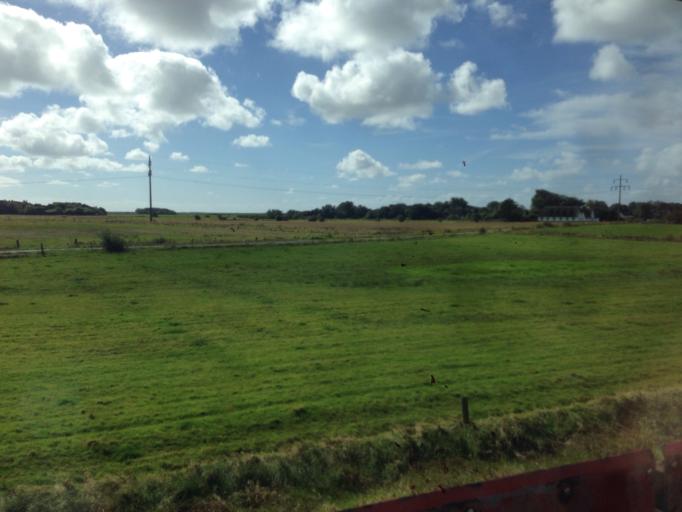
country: DE
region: Schleswig-Holstein
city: Sylt-Ost
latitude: 54.8767
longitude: 8.4062
